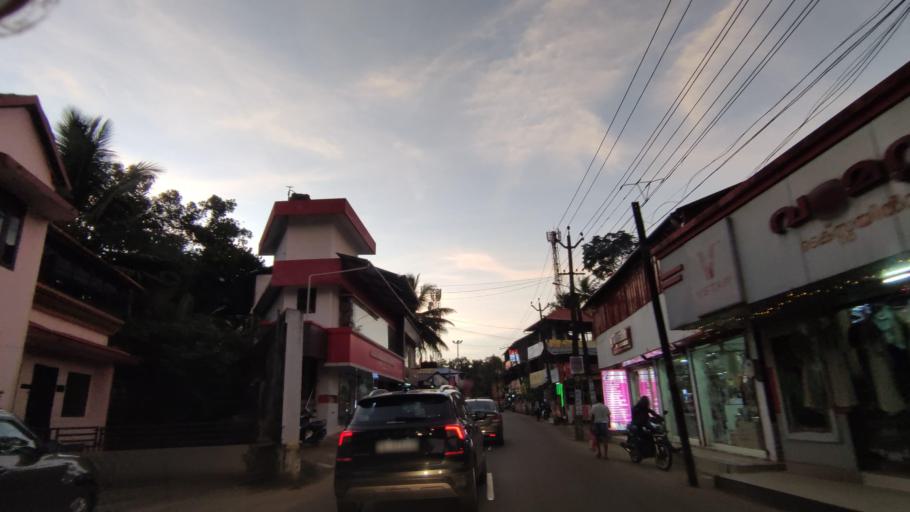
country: IN
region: Kerala
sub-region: Kottayam
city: Vaikam
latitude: 9.6975
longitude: 76.4787
